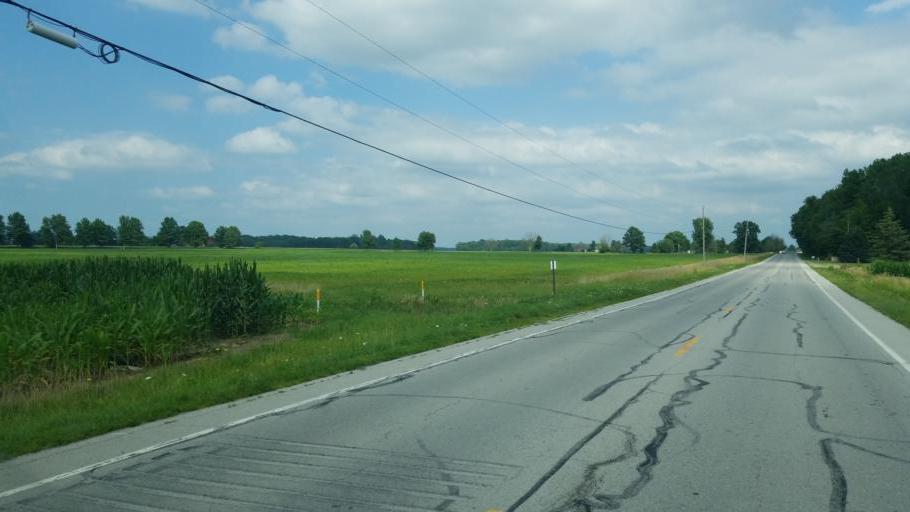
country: US
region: Ohio
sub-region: Crawford County
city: Crestline
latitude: 40.8068
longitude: -82.7841
